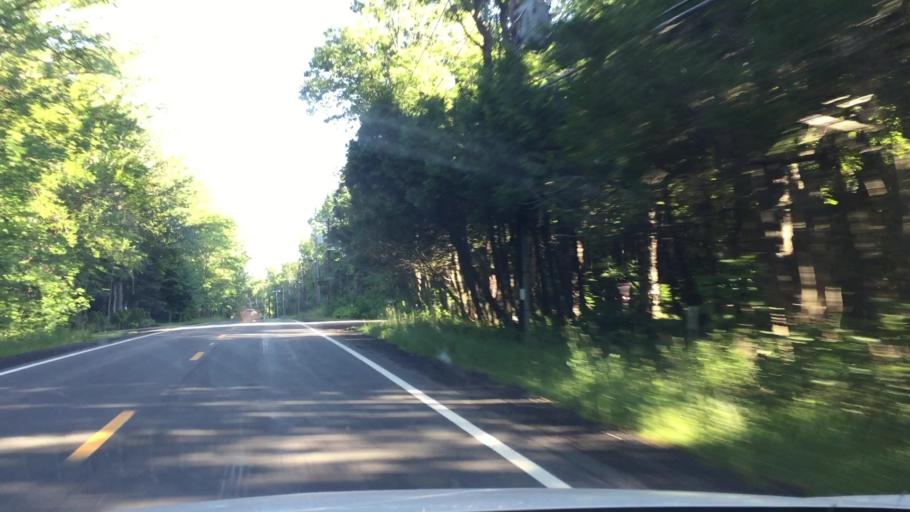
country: US
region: Massachusetts
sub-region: Berkshire County
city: Becket
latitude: 42.3005
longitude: -73.0611
